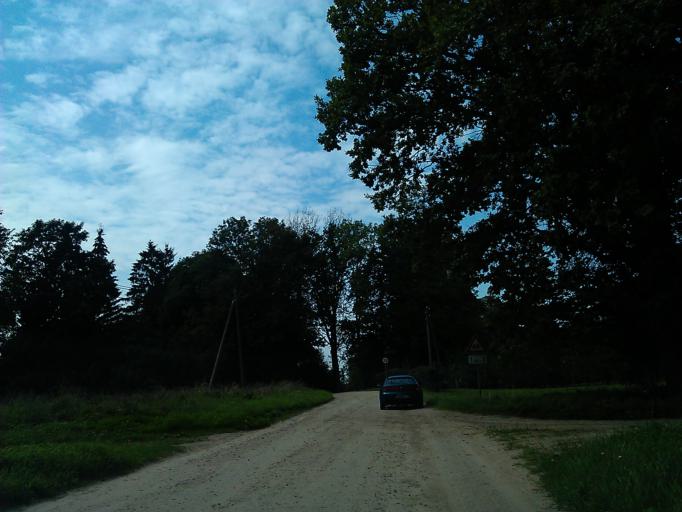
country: LV
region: Lecava
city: Iecava
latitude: 56.6815
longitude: 24.2488
